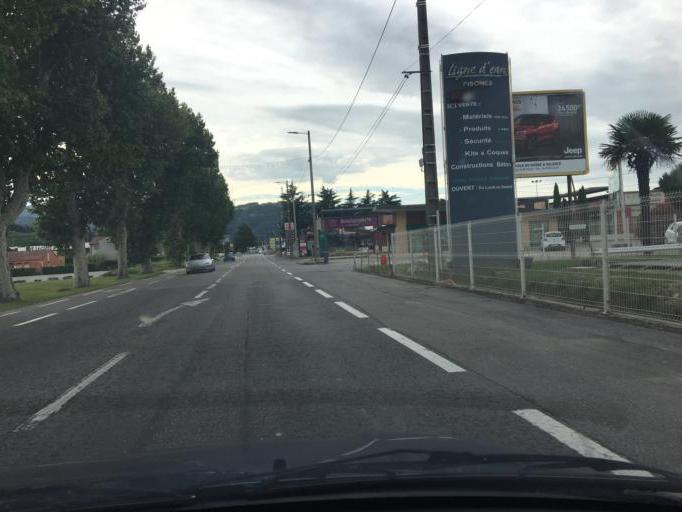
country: FR
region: Rhone-Alpes
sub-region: Departement de l'Ardeche
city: Saint-Peray
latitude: 44.9421
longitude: 4.8607
